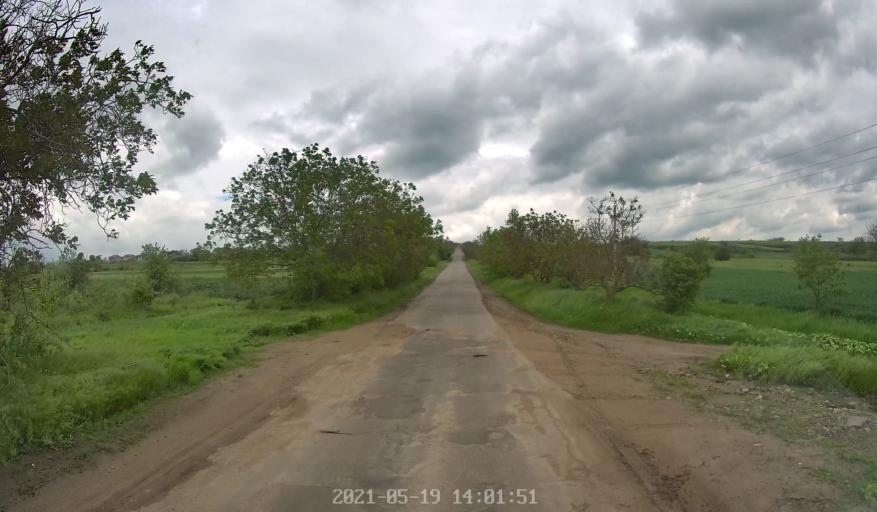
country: MD
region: Chisinau
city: Chisinau
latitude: 47.0331
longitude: 28.9402
